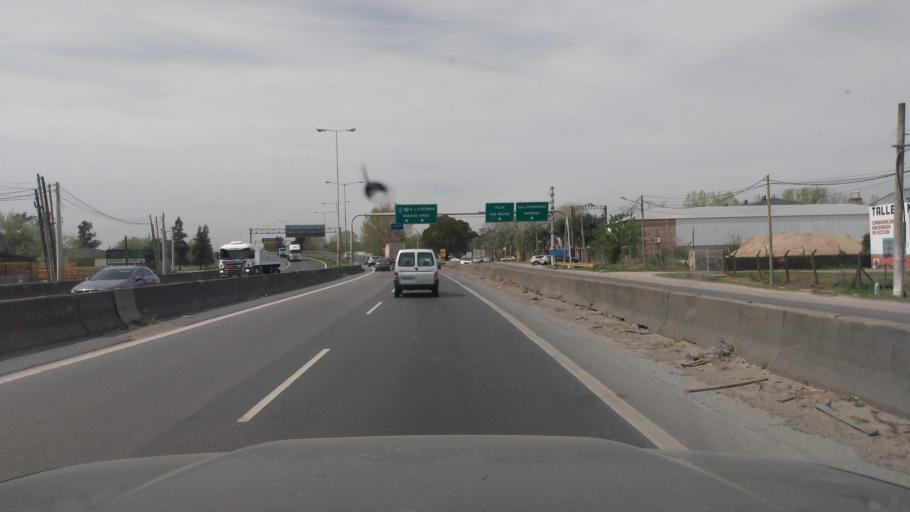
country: AR
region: Buenos Aires
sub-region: Partido de Pilar
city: Pilar
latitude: -34.4527
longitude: -58.9437
